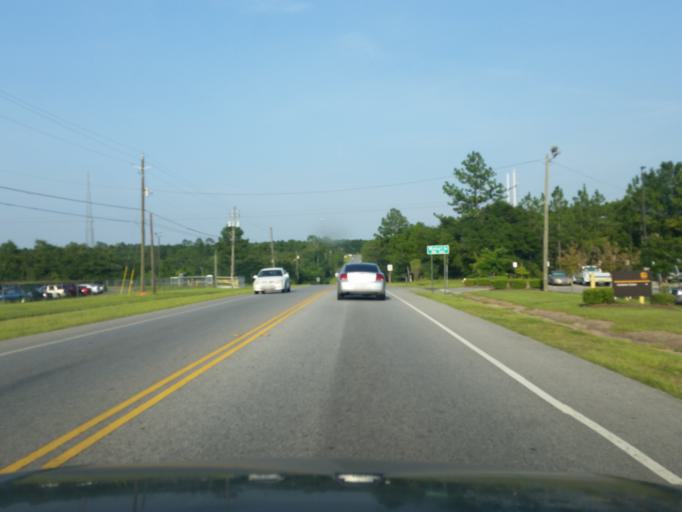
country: US
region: Florida
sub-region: Escambia County
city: Bellview
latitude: 30.4863
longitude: -87.2911
